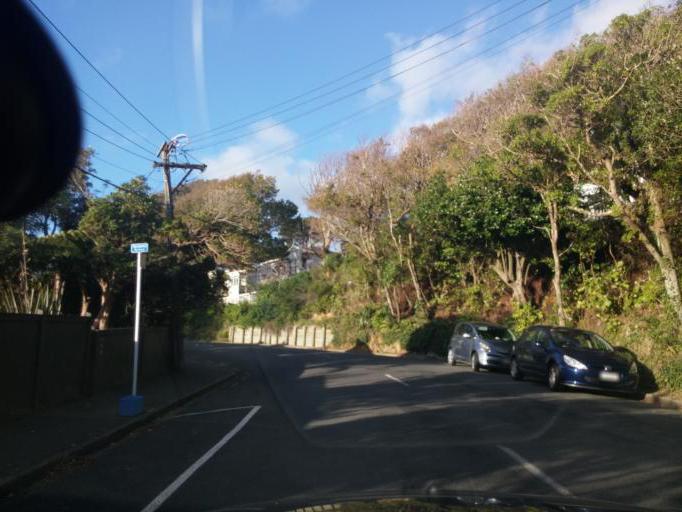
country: NZ
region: Wellington
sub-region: Wellington City
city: Kelburn
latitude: -41.2887
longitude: 174.7646
